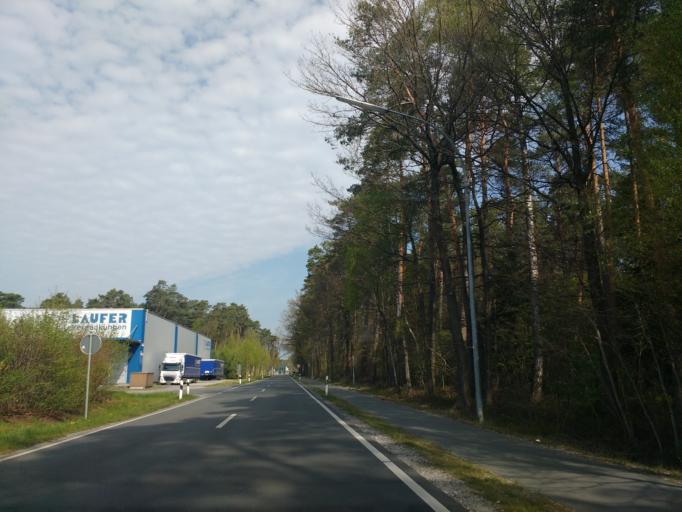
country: DE
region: North Rhine-Westphalia
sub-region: Regierungsbezirk Detmold
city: Hovelhof
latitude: 51.8340
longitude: 8.6559
